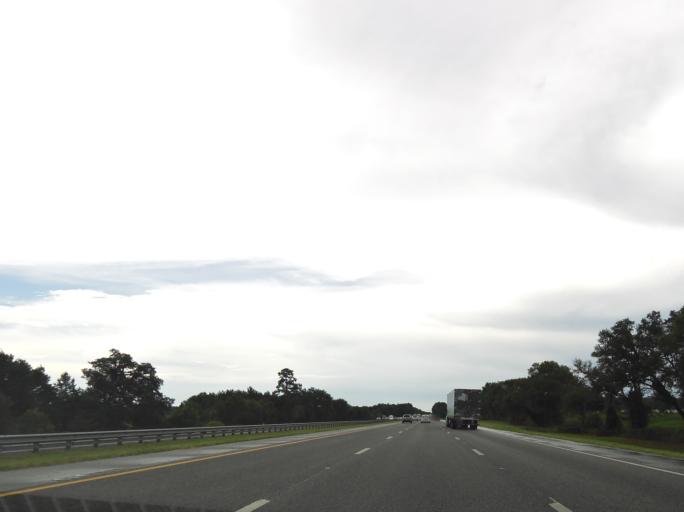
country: US
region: Florida
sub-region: Hamilton County
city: Jasper
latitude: 30.4893
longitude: -83.0161
